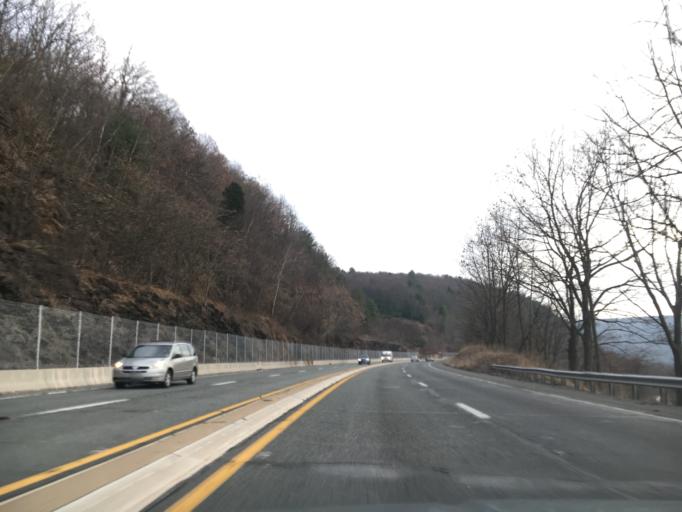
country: US
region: Pennsylvania
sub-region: Carbon County
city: Weissport East
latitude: 40.8141
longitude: -75.6706
